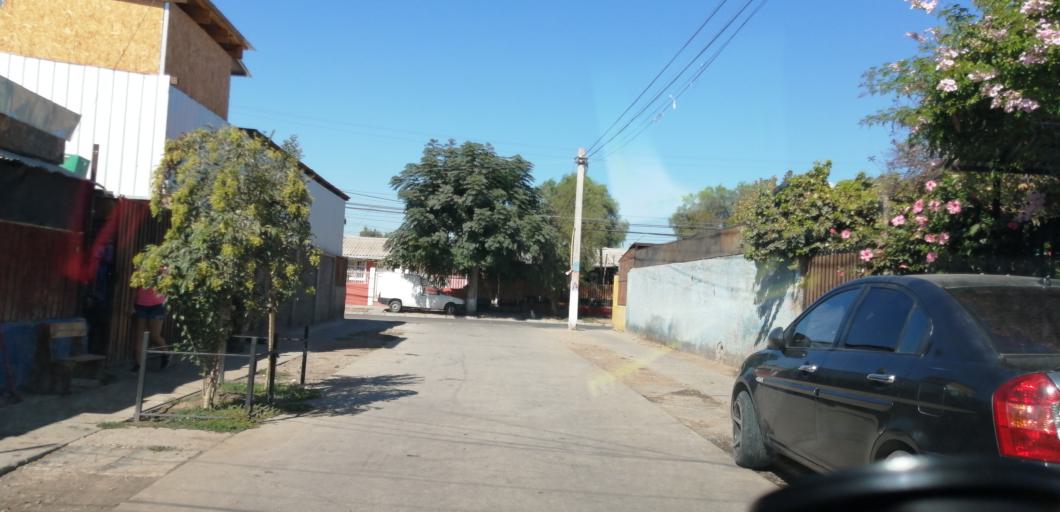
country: CL
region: Santiago Metropolitan
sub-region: Provincia de Santiago
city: Lo Prado
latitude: -33.4321
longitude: -70.7591
